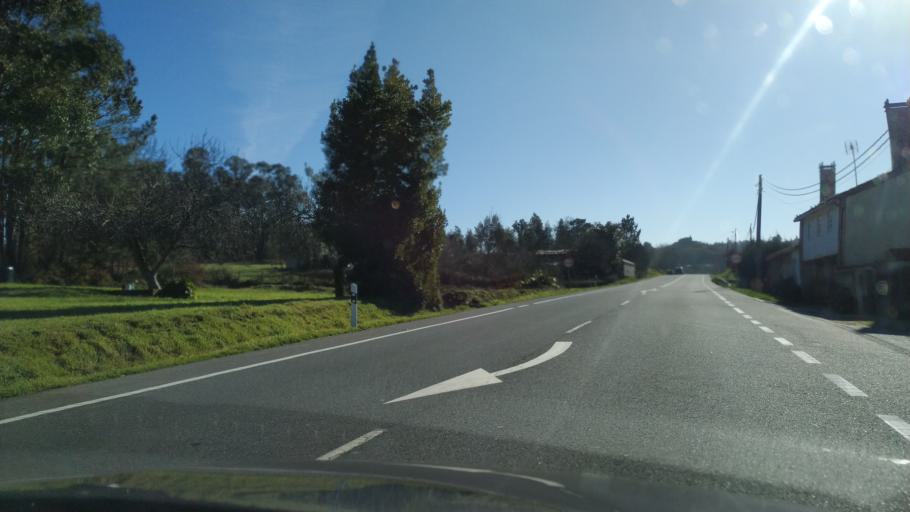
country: ES
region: Galicia
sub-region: Provincia da Coruna
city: Ribeira
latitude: 42.7514
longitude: -8.3512
